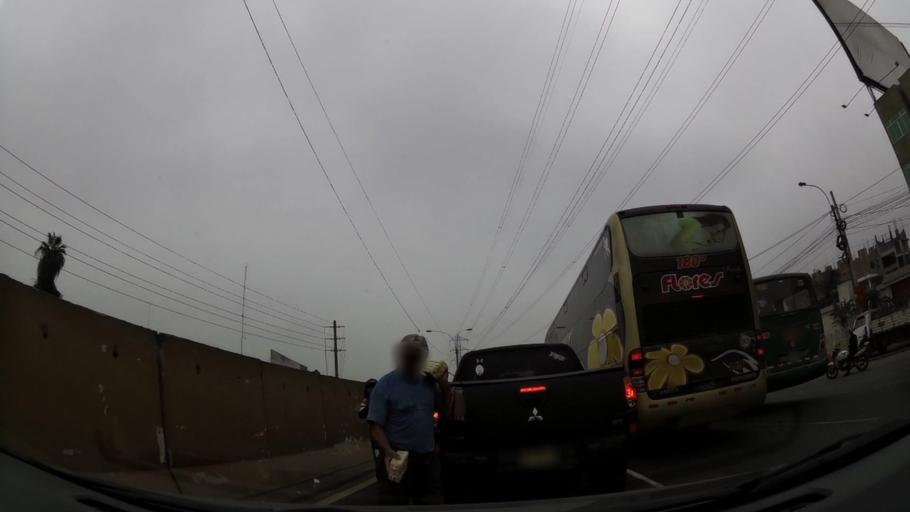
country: PE
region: Lima
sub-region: Lima
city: Urb. Santo Domingo
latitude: -11.9124
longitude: -77.0732
